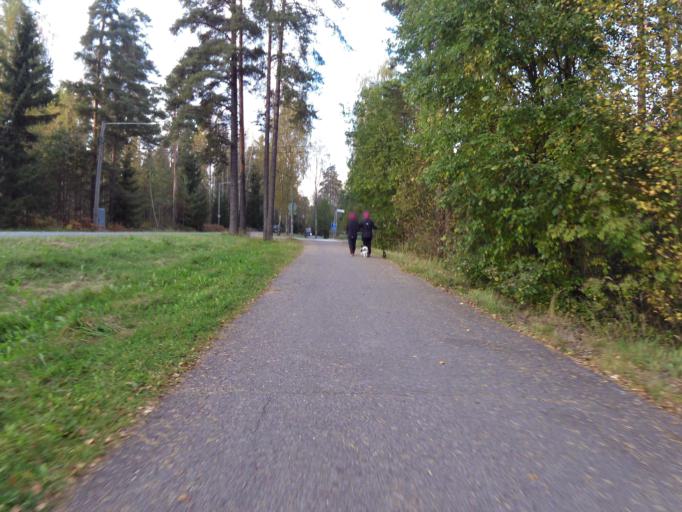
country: FI
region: Uusimaa
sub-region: Helsinki
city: Kauniainen
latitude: 60.2854
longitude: 24.7465
